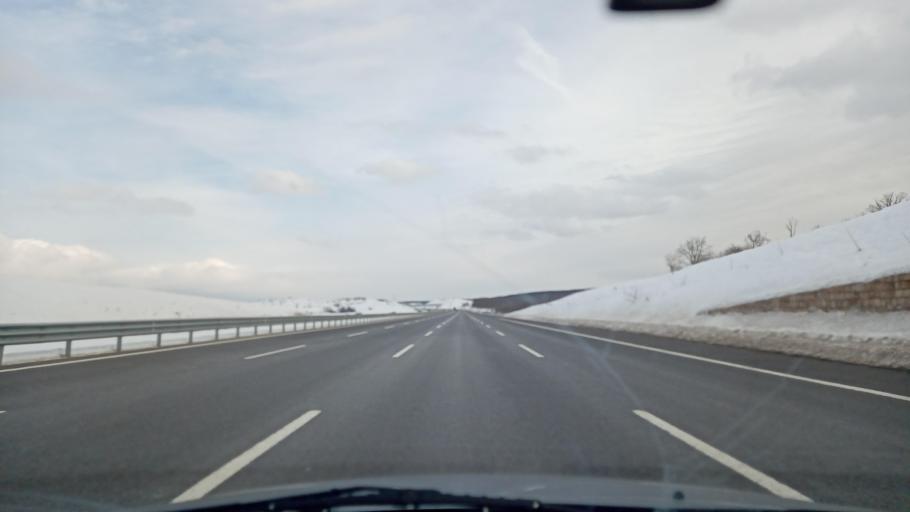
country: TR
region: Kocaeli
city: Hereke
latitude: 40.8932
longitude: 29.6101
